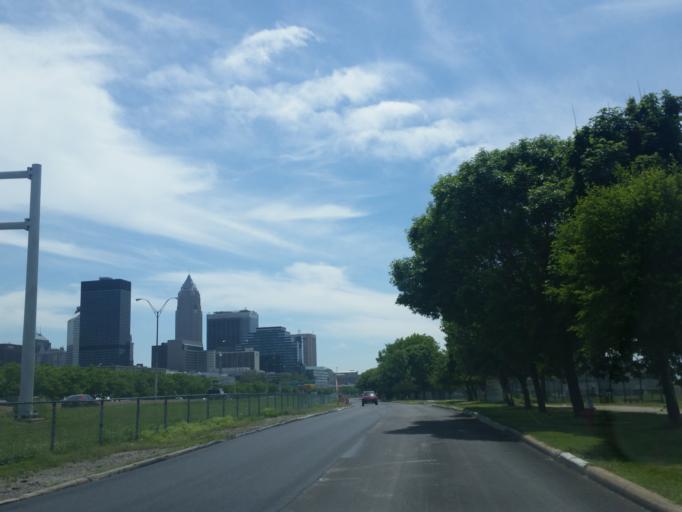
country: US
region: Ohio
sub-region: Cuyahoga County
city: Cleveland
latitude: 41.5145
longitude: -81.6827
